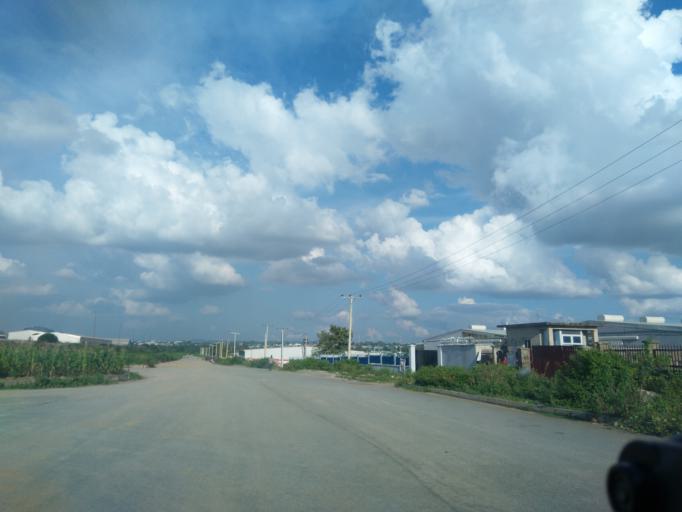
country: NG
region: Abuja Federal Capital Territory
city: Abuja
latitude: 9.0295
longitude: 7.4042
